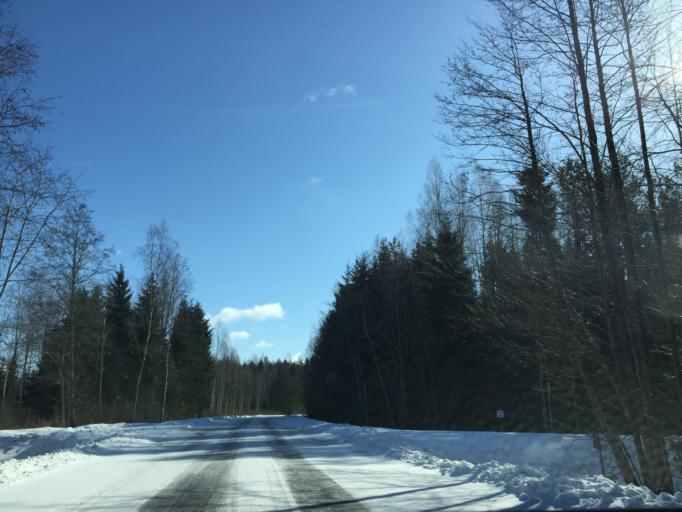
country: LV
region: Salacgrivas
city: Ainazi
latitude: 57.9977
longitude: 24.5606
